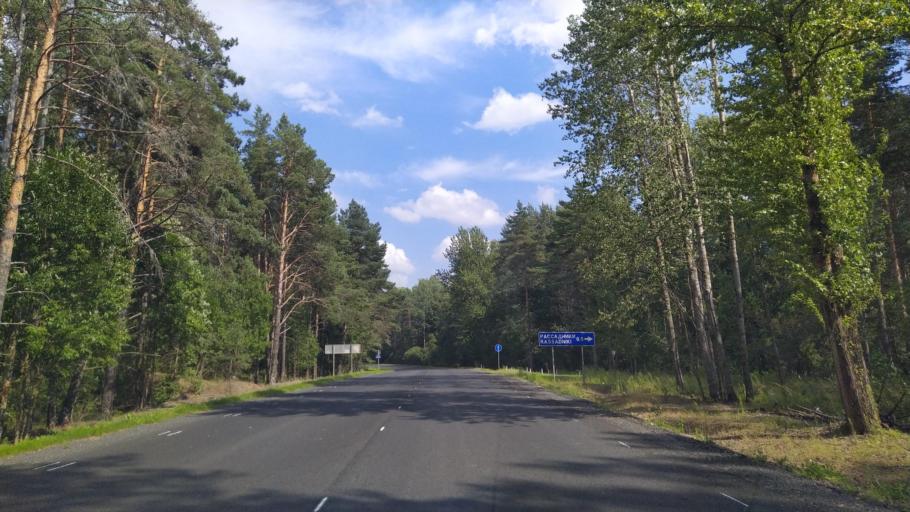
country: RU
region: Pskov
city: Porkhov
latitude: 57.7168
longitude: 29.2236
